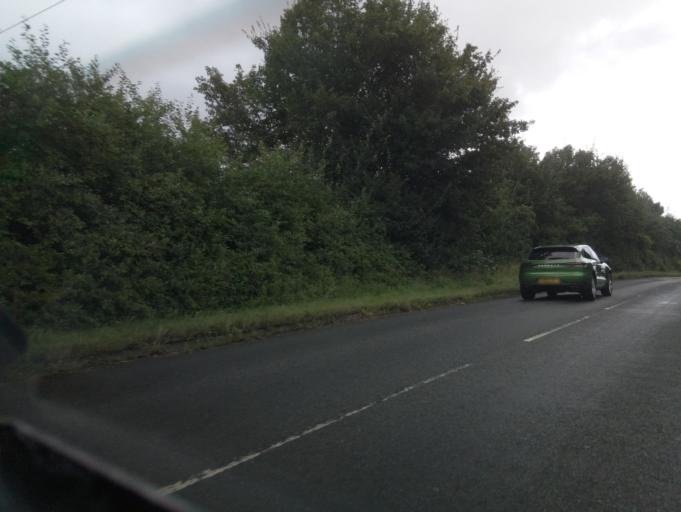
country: GB
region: England
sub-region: Solihull
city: Cheswick Green
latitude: 52.3862
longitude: -1.8233
